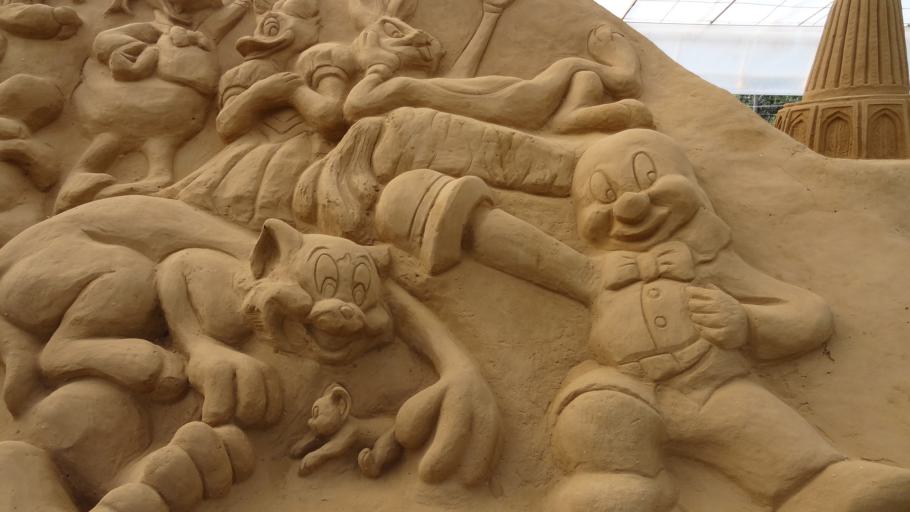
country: IN
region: Karnataka
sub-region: Mysore
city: Mysore
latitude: 12.2950
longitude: 76.6822
